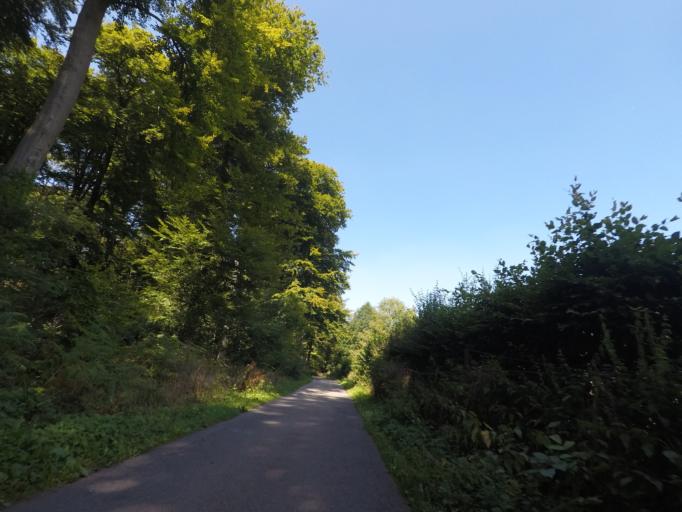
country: LU
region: Luxembourg
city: Bereldange
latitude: 49.6467
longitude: 6.1126
